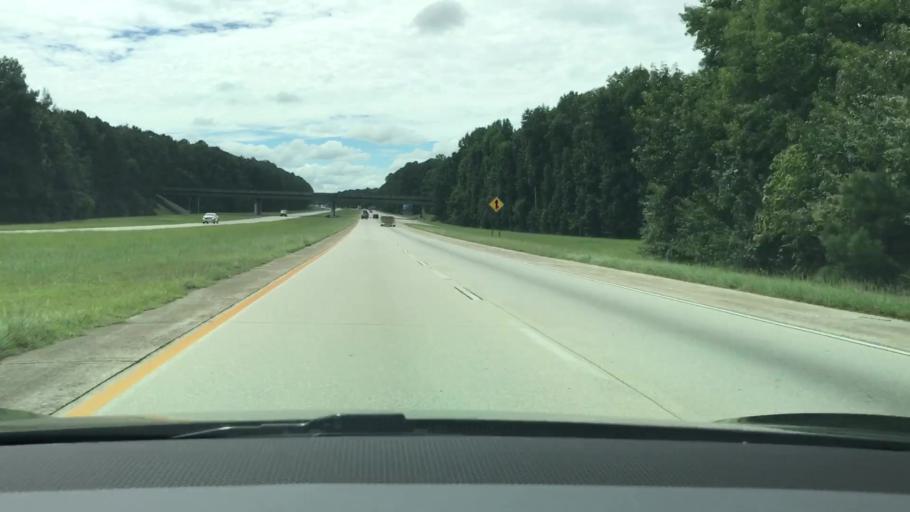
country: US
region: Georgia
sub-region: Troup County
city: La Grange
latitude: 33.0597
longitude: -84.9476
